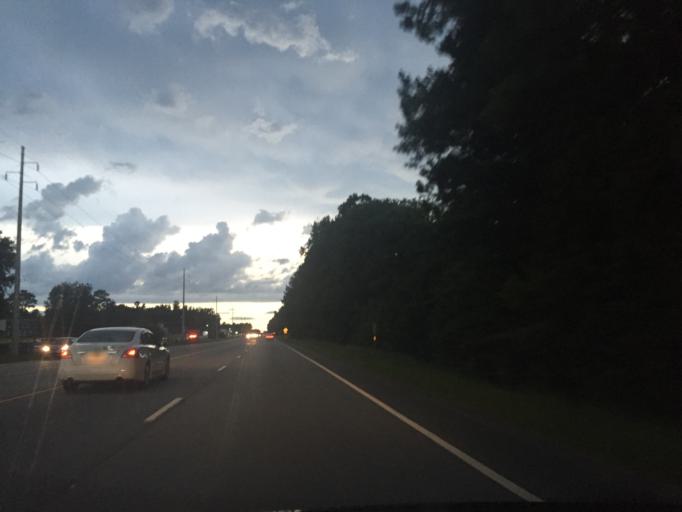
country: US
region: Georgia
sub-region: Liberty County
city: Hinesville
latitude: 31.8384
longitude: -81.5390
